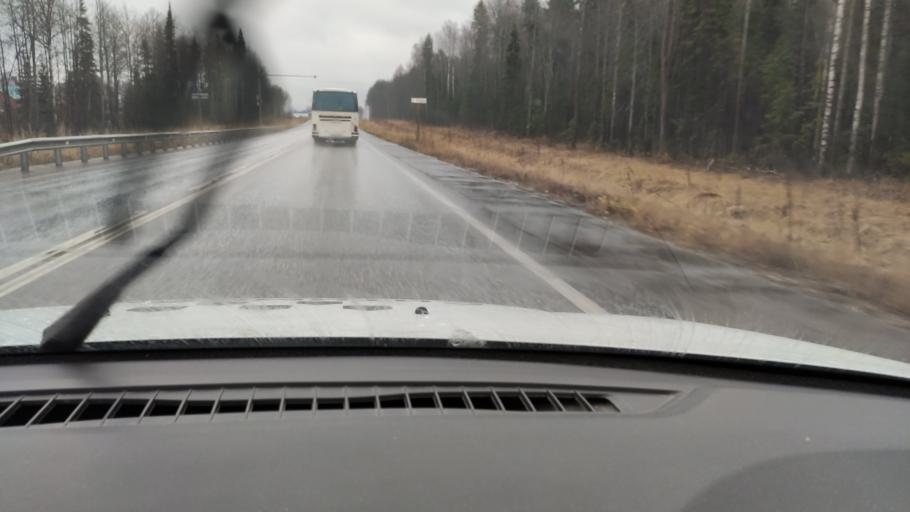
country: RU
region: Perm
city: Novyye Lyady
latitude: 58.0482
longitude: 56.5692
